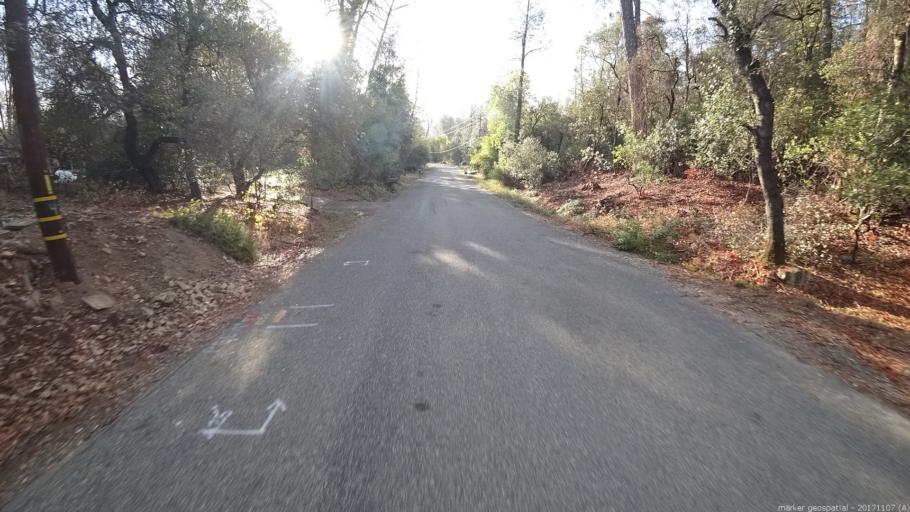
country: US
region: California
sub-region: Shasta County
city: Shasta
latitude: 40.5812
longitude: -122.4696
